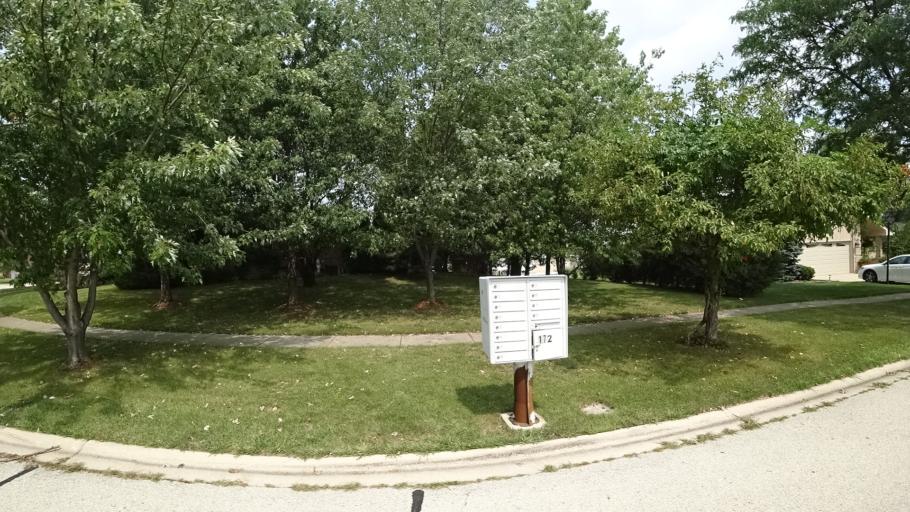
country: US
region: Illinois
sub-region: Will County
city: Goodings Grove
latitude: 41.6214
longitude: -87.9101
